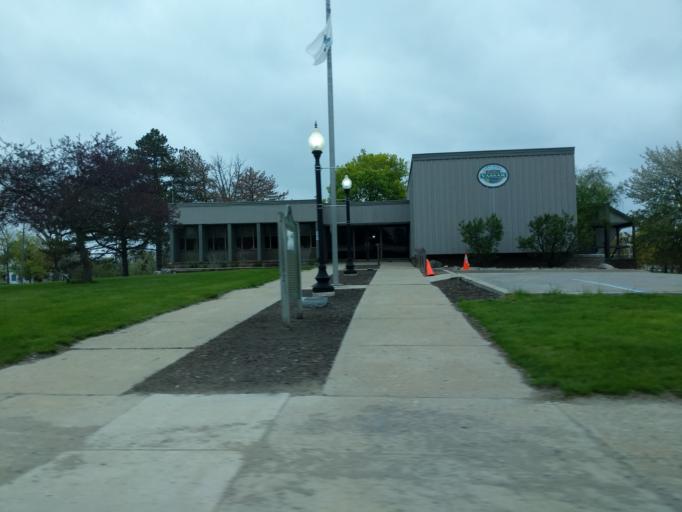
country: US
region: Michigan
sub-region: Tuscola County
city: Vassar
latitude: 43.3706
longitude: -83.5802
